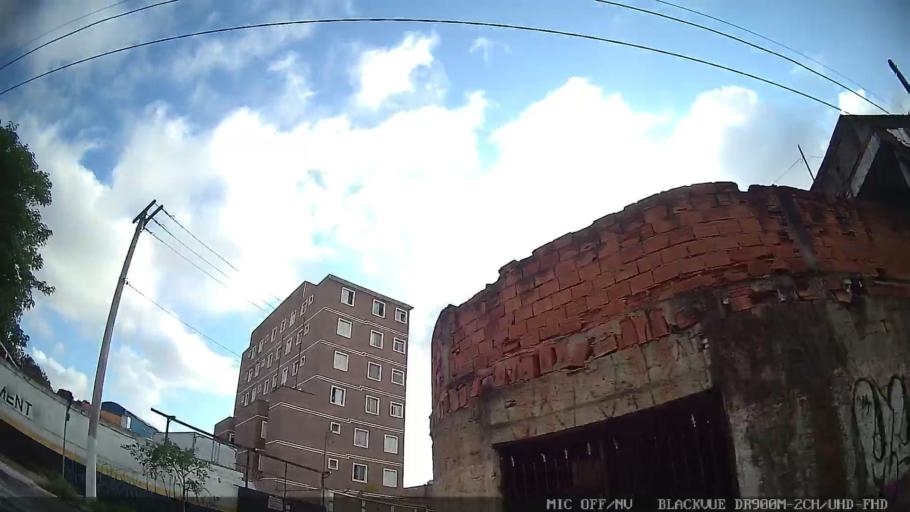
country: BR
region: Sao Paulo
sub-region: Guarulhos
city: Guarulhos
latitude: -23.5362
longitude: -46.5191
